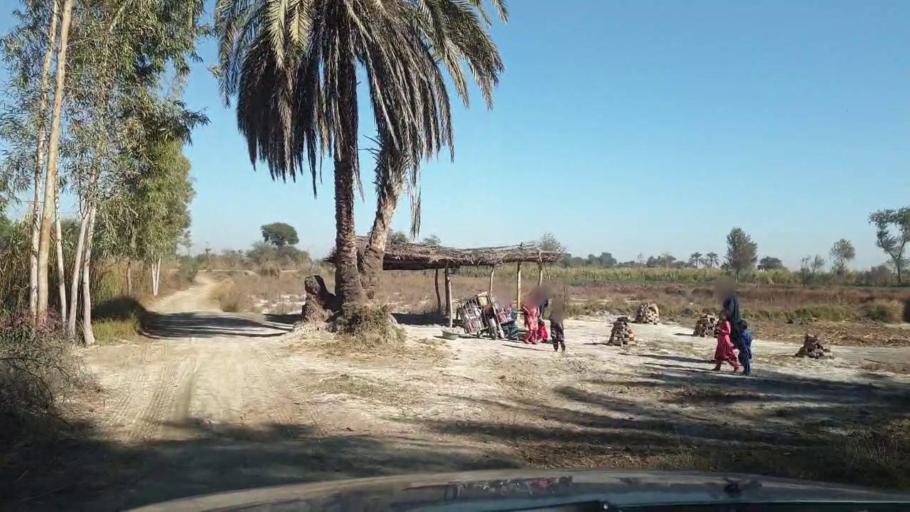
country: PK
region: Sindh
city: Ghotki
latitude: 28.0344
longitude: 69.2890
